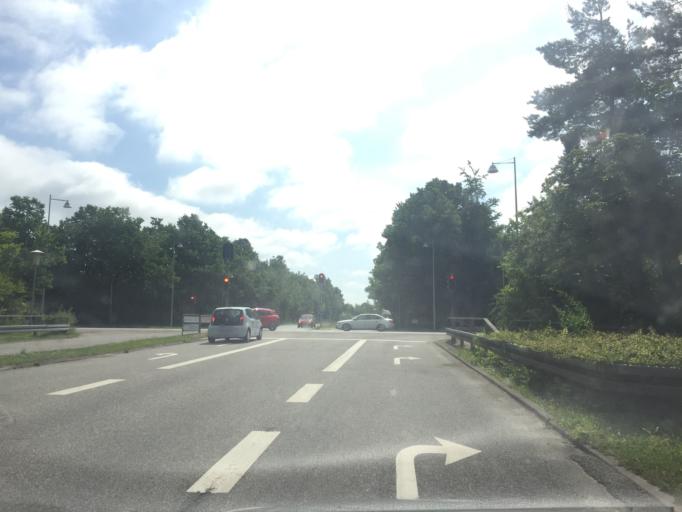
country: DK
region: Capital Region
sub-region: Albertslund Kommune
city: Albertslund
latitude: 55.6735
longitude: 12.3406
